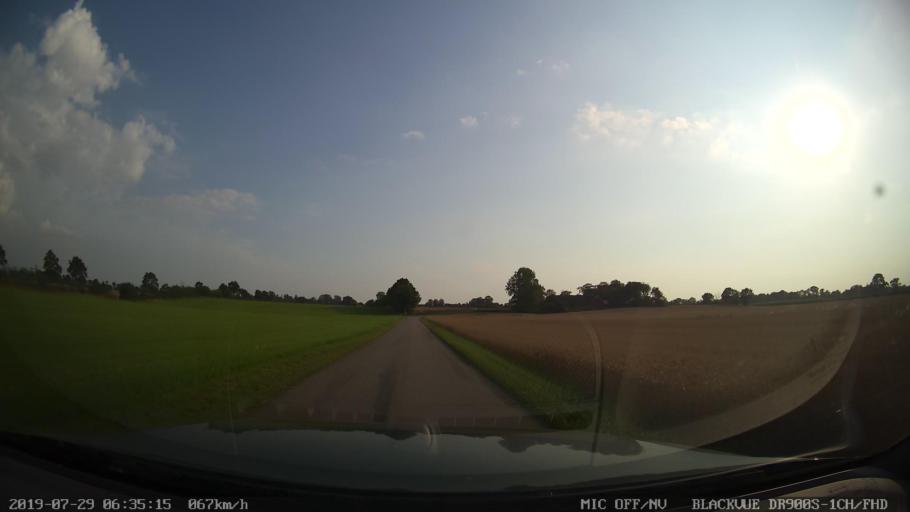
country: SE
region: Skane
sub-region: Helsingborg
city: Odakra
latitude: 56.1143
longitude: 12.7194
